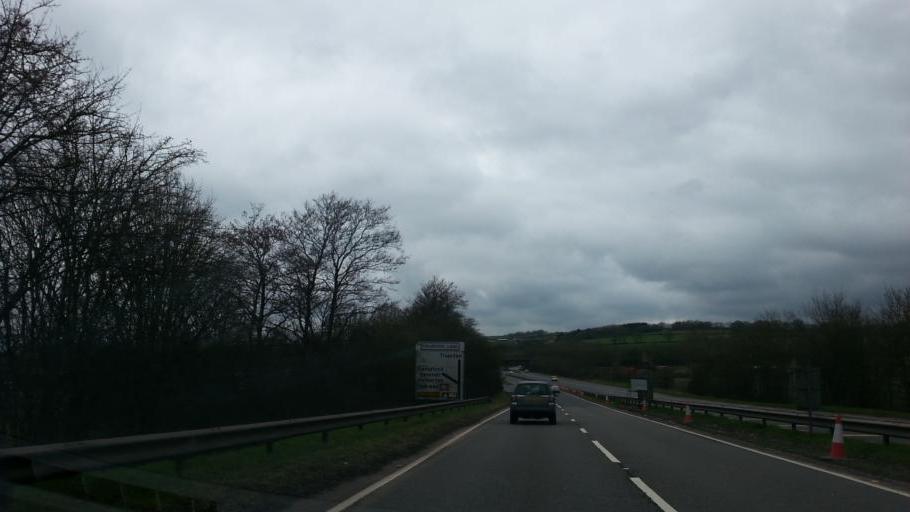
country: GB
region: England
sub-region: Devon
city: Uffculme
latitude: 50.9198
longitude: -3.3611
